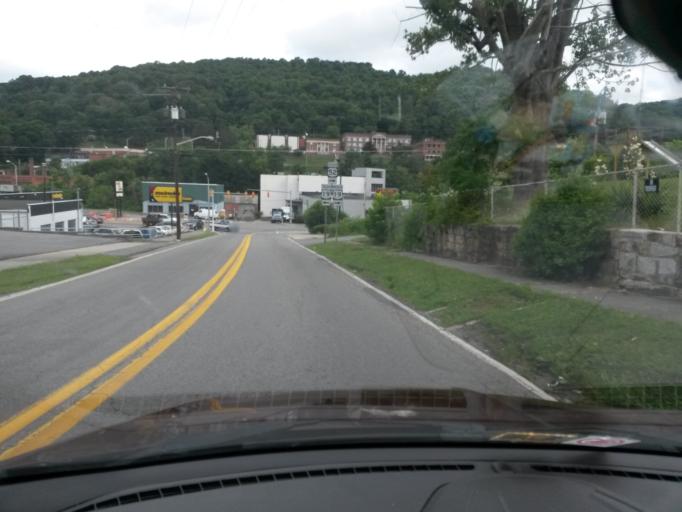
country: US
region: West Virginia
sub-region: Mercer County
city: Bluefield
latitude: 37.2640
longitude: -81.2354
